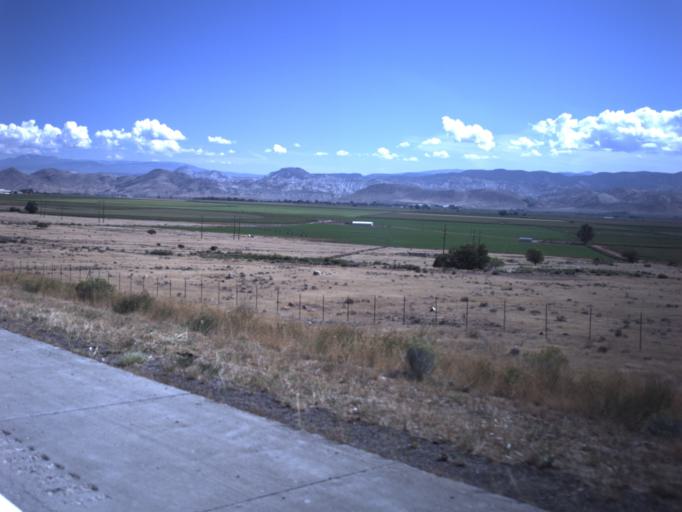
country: US
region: Utah
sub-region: Sevier County
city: Richfield
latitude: 38.8278
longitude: -112.0381
